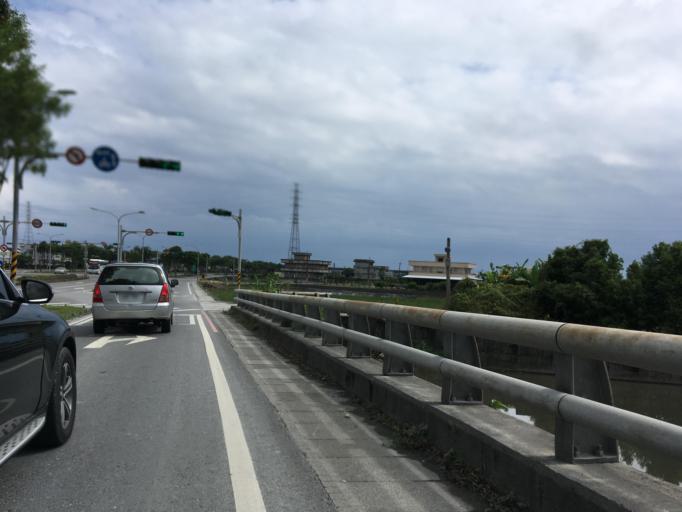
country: TW
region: Taiwan
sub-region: Yilan
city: Yilan
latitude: 24.6780
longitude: 121.7849
